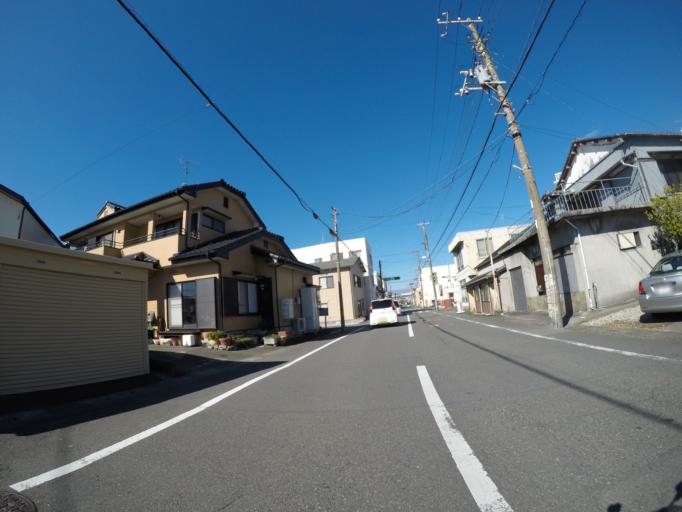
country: JP
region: Shizuoka
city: Fuji
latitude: 35.1441
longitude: 138.7045
